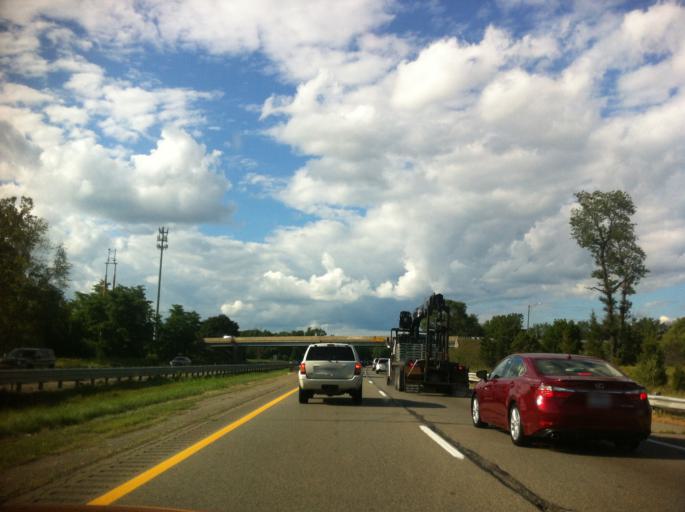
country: US
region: Michigan
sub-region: Livingston County
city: Whitmore Lake
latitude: 42.3931
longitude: -83.7634
